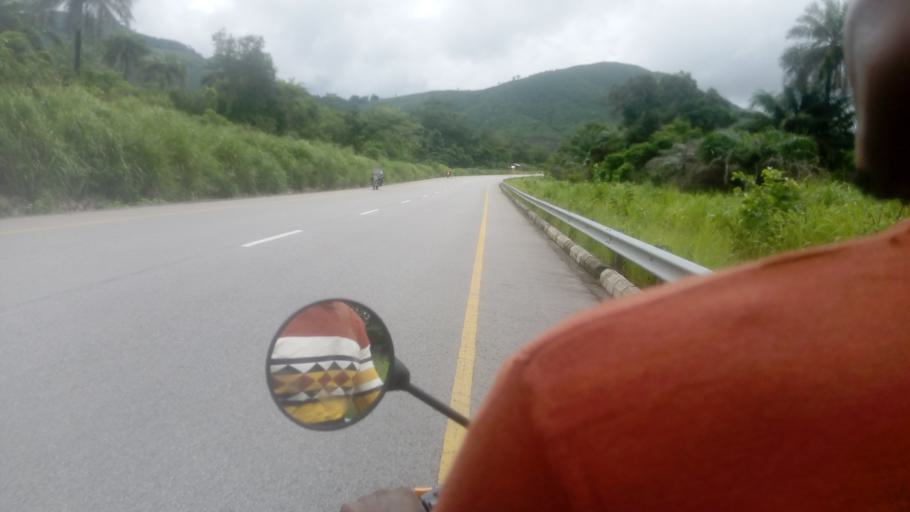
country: SL
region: Northern Province
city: Masaka
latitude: 8.6604
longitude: -11.8024
